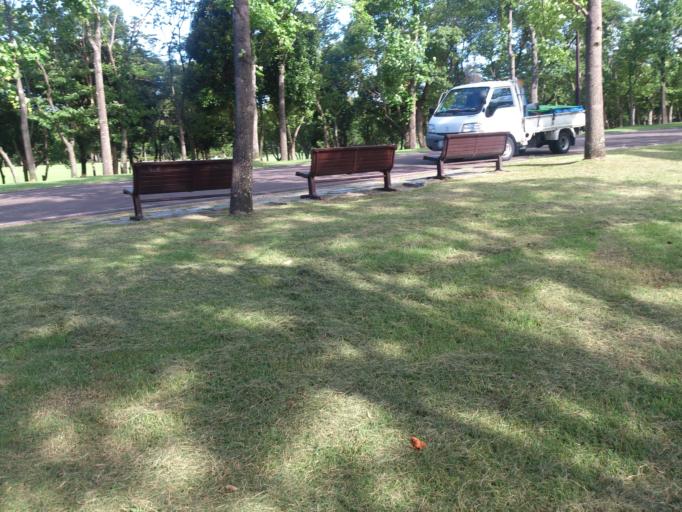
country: JP
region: Hyogo
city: Kobe
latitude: 34.7104
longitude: 135.1152
